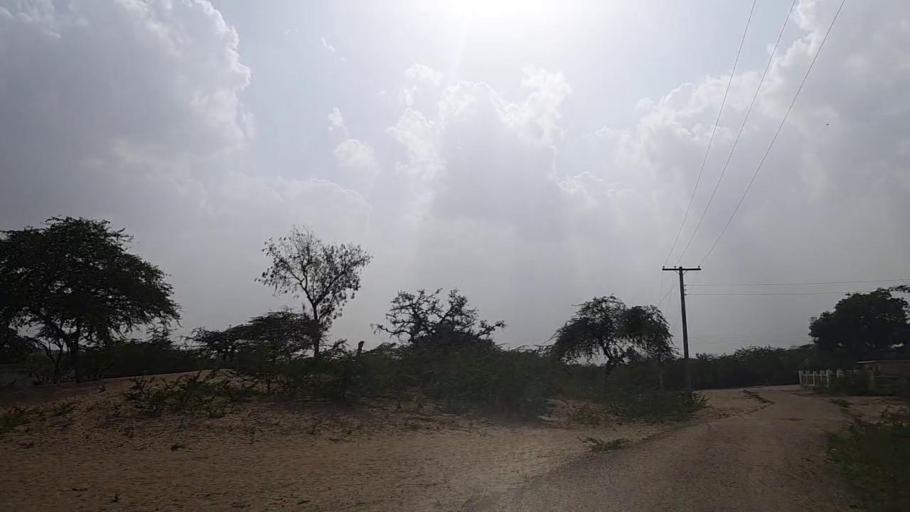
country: PK
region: Sindh
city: Islamkot
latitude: 24.8696
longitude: 70.1665
